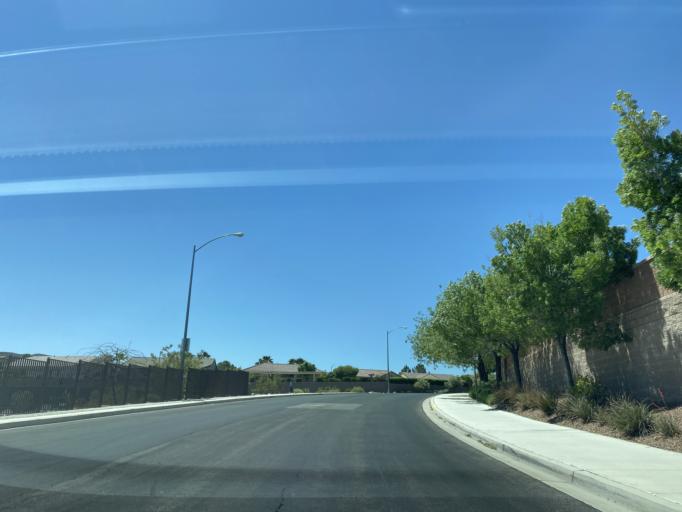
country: US
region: Nevada
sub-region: Clark County
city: Whitney
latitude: 35.9451
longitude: -115.0842
